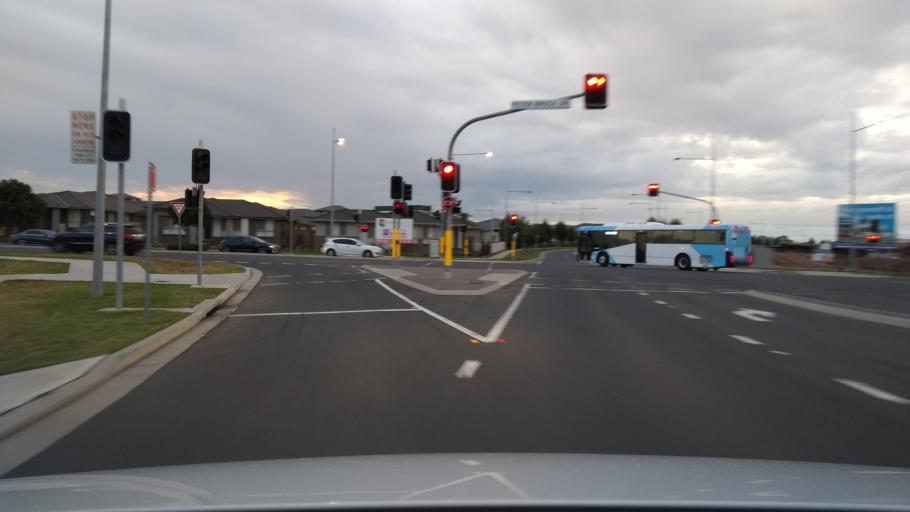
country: AU
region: New South Wales
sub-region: Camden
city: Narellan
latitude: -34.0020
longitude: 150.7353
